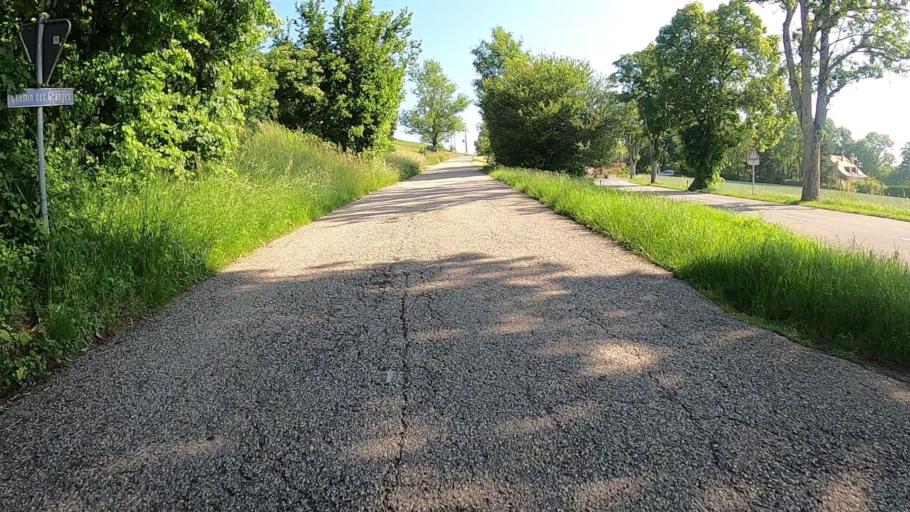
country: CH
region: Vaud
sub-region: Nyon District
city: Rolle
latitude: 46.4804
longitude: 6.3356
